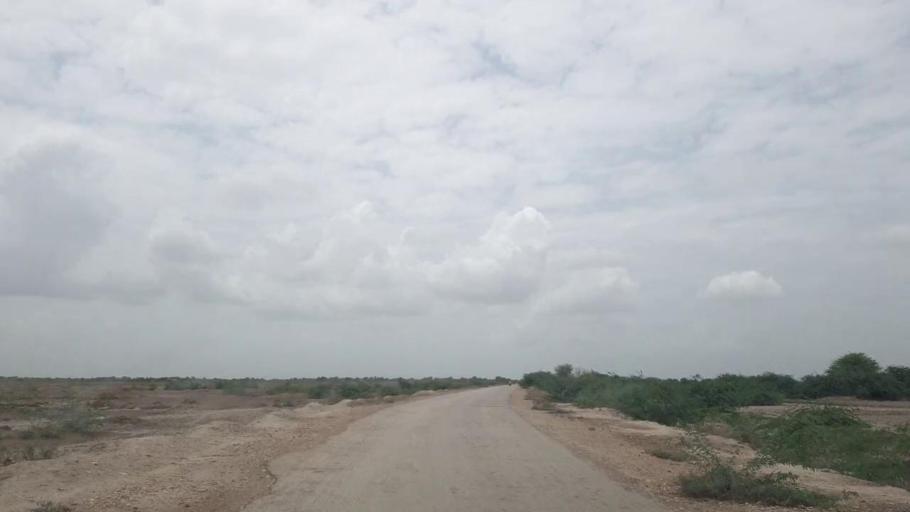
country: PK
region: Sindh
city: Naukot
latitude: 24.9505
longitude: 69.2822
